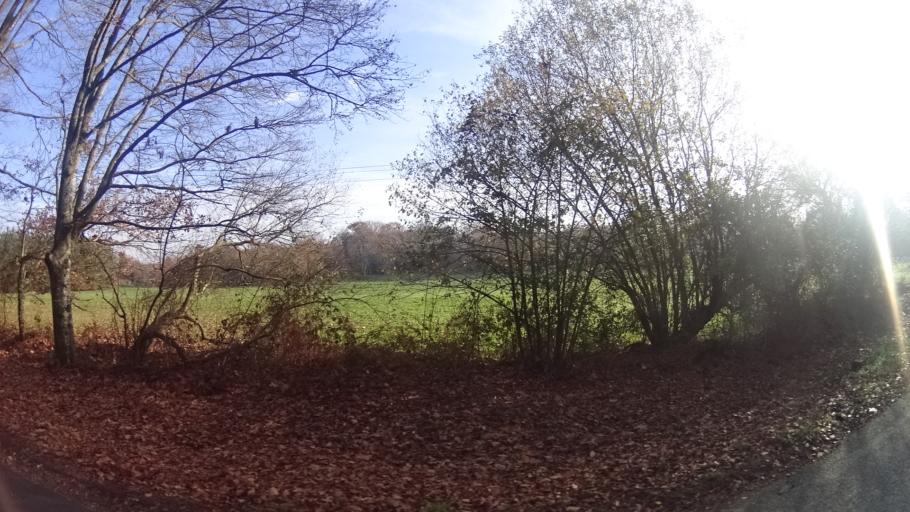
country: FR
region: Brittany
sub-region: Departement du Morbihan
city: Allaire
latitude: 47.6356
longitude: -2.1529
